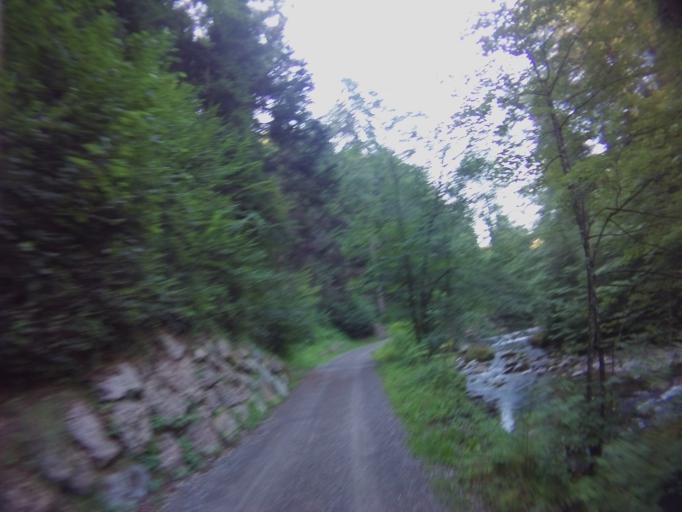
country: CH
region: Zug
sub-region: Zug
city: Menzingen
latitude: 47.1654
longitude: 8.5602
